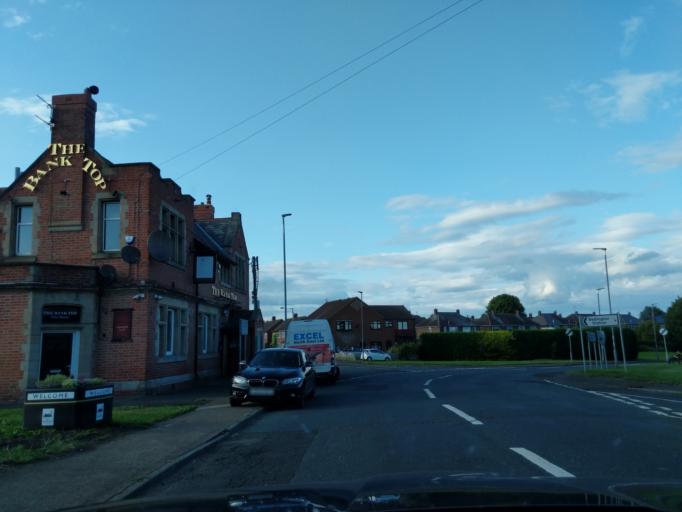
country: GB
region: England
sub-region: Northumberland
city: Bedlington
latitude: 55.1343
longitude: -1.5677
